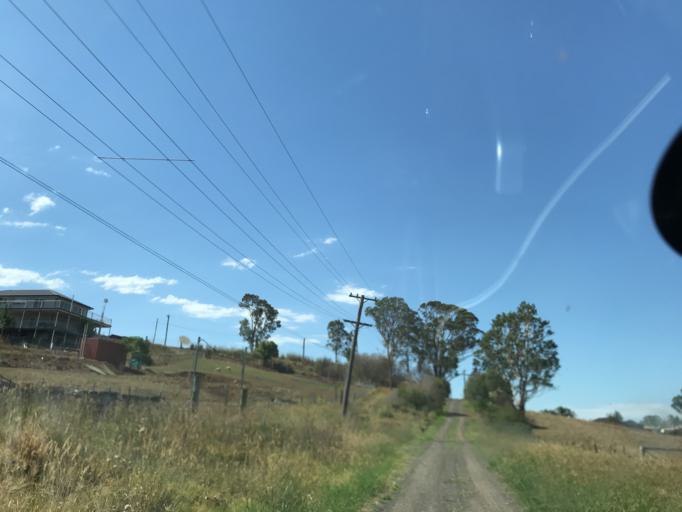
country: AU
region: New South Wales
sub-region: Penrith Municipality
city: Kingswood Park
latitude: -33.7943
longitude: 150.7373
